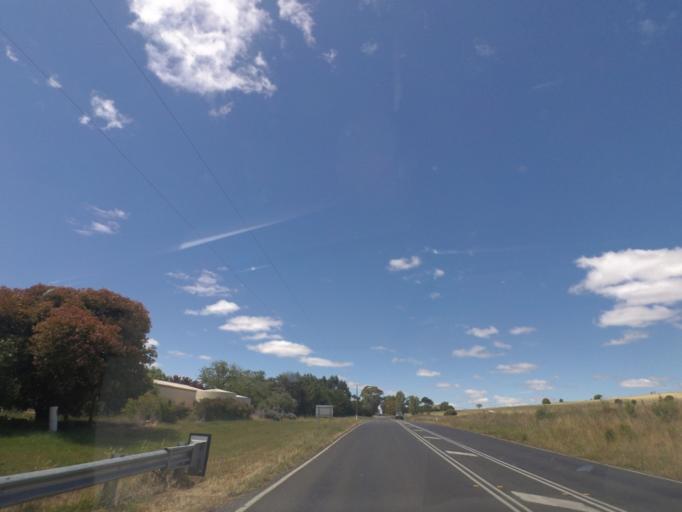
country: AU
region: Victoria
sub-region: Mount Alexander
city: Castlemaine
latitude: -37.3233
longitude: 144.1950
